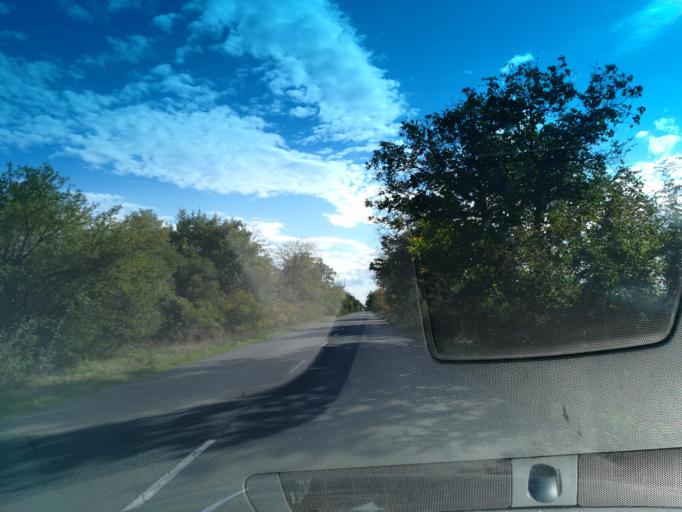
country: BG
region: Stara Zagora
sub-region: Obshtina Stara Zagora
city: Stara Zagora
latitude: 42.3731
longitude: 25.6524
